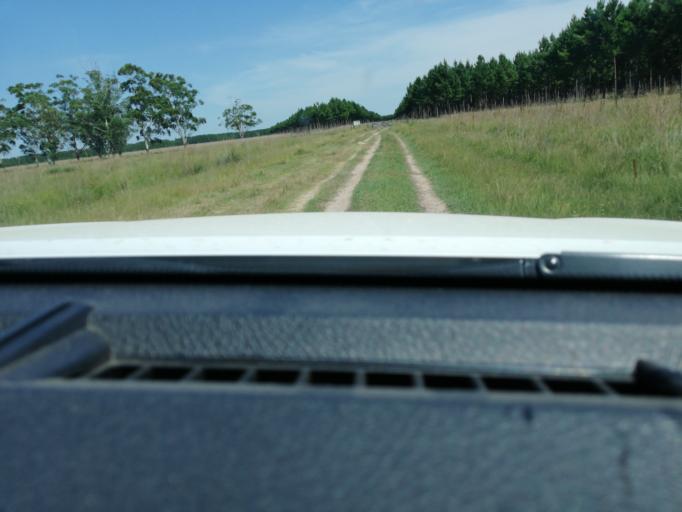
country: AR
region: Corrientes
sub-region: Departamento de San Miguel
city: San Miguel
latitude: -28.0375
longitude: -57.4635
